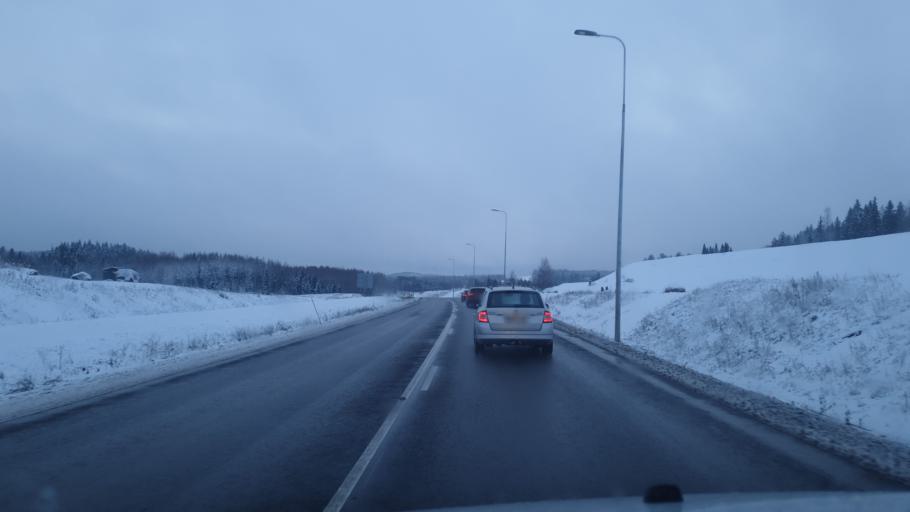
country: FI
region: Central Finland
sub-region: Jyvaeskylae
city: Jyvaeskylae
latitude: 62.3477
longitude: 25.7041
